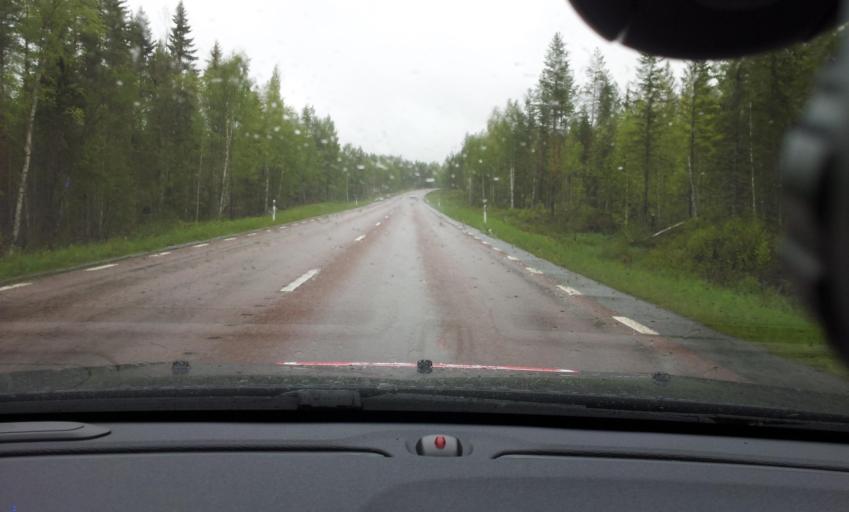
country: SE
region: Jaemtland
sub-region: Bergs Kommun
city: Hoverberg
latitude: 62.8191
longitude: 14.5166
